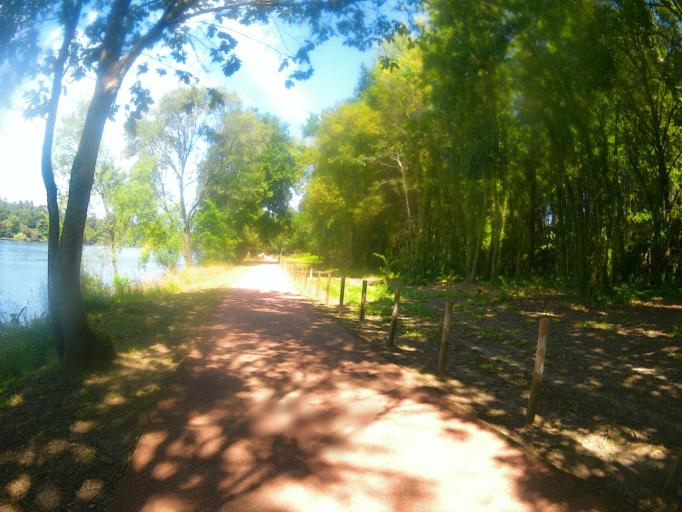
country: PT
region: Viana do Castelo
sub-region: Valenca
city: Valenca
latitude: 41.9928
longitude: -8.6744
